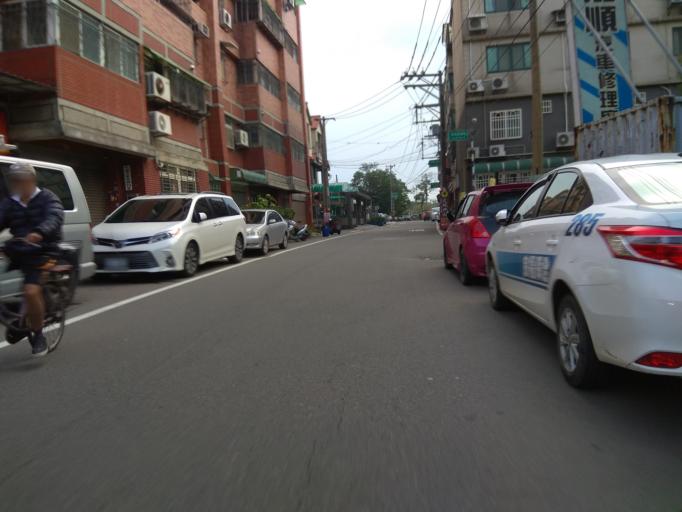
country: TW
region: Taiwan
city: Taoyuan City
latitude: 24.9445
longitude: 121.2007
